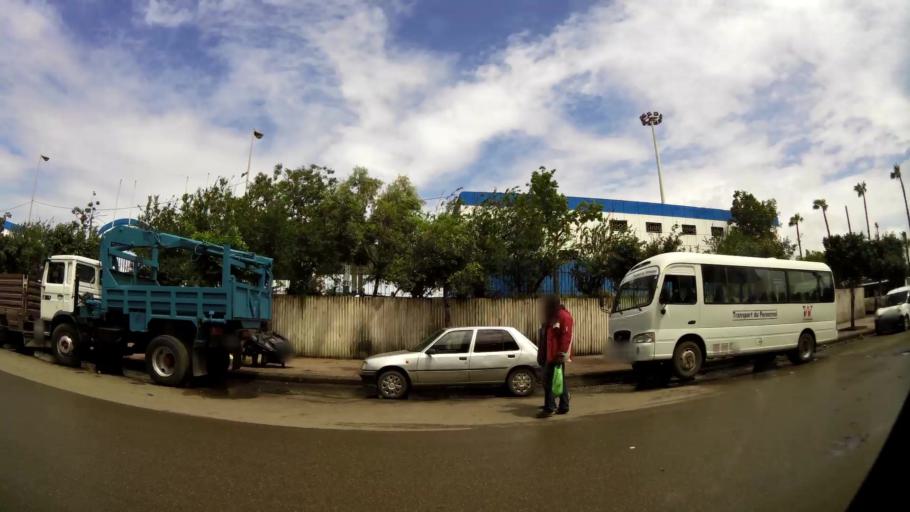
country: MA
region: Grand Casablanca
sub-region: Casablanca
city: Casablanca
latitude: 33.5734
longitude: -7.5886
